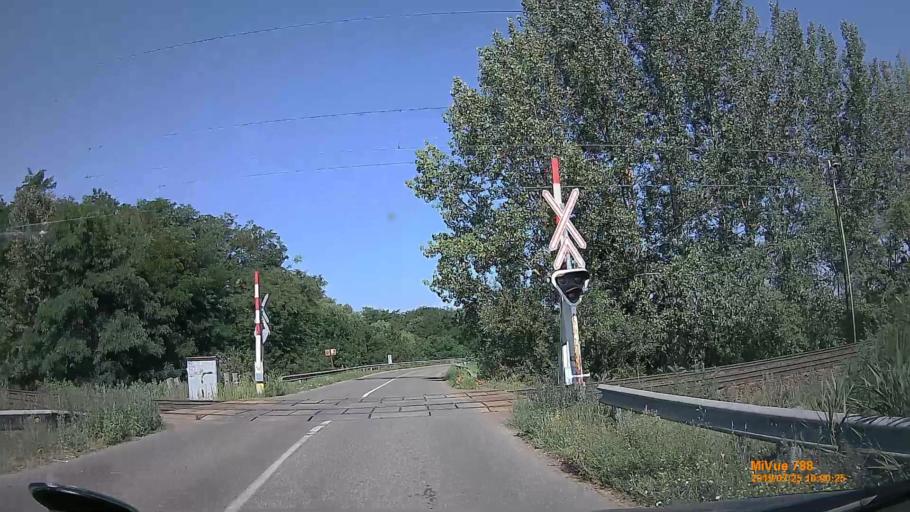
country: HU
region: Szabolcs-Szatmar-Bereg
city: Kotaj
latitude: 48.0294
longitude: 21.7575
